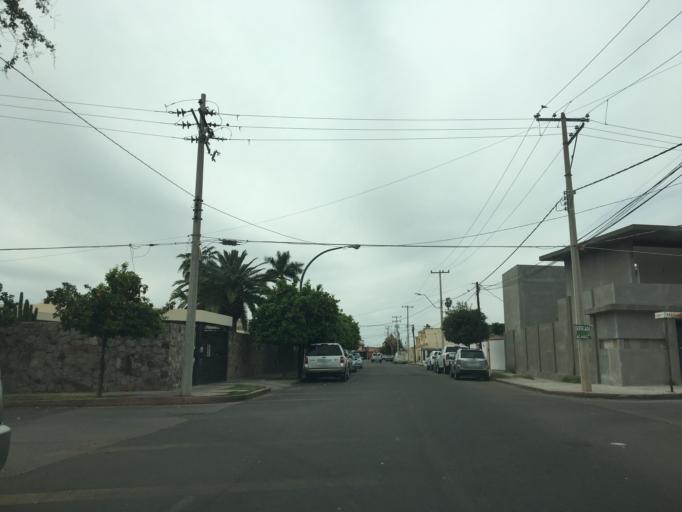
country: MX
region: Sonora
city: Hermosillo
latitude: 29.0756
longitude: -110.9663
